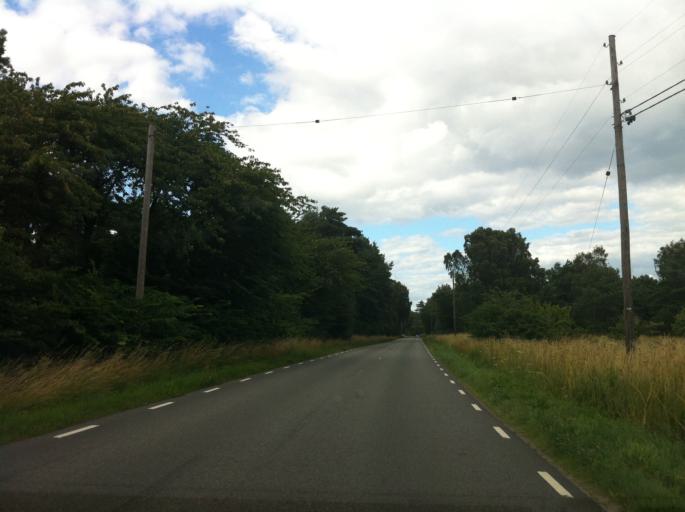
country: SE
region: Skane
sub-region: Simrishamns Kommun
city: Simrishamn
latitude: 55.4229
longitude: 14.2145
